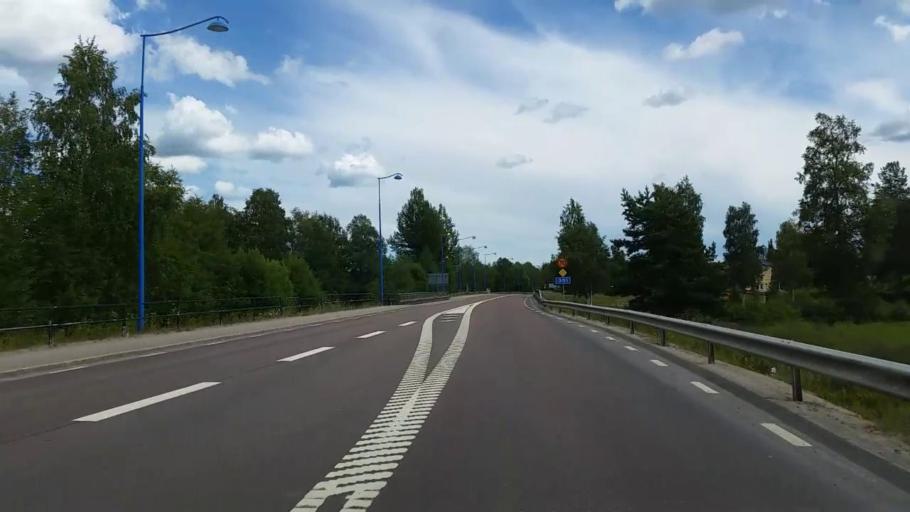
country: SE
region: Gaevleborg
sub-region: Ovanakers Kommun
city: Edsbyn
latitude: 61.3835
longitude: 15.8236
